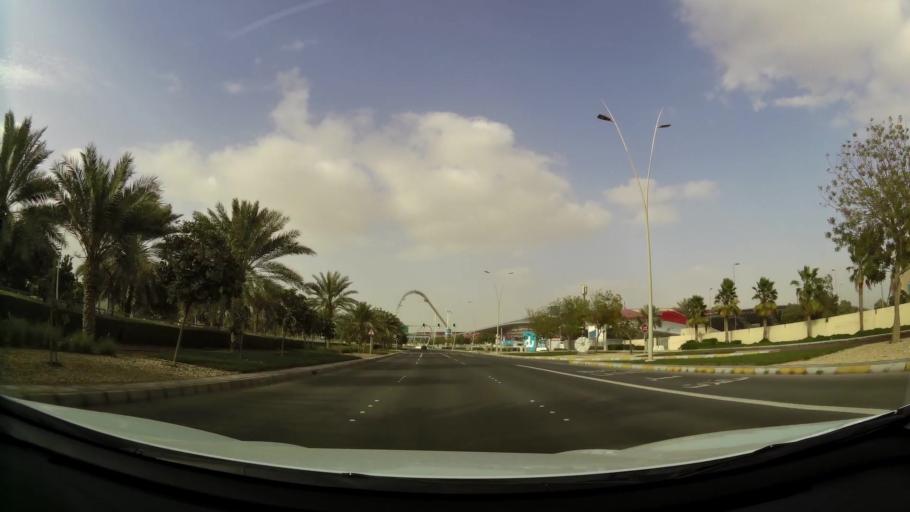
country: AE
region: Abu Dhabi
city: Abu Dhabi
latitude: 24.4794
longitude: 54.6039
